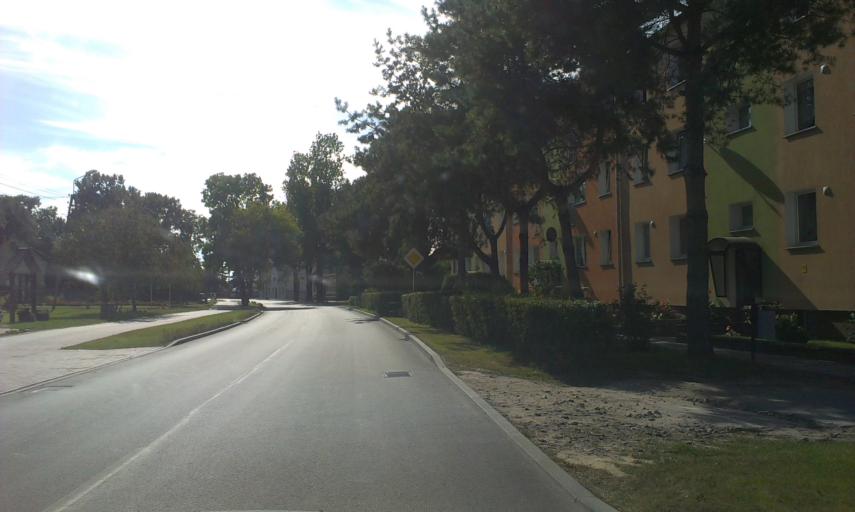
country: PL
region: Greater Poland Voivodeship
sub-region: Powiat pilski
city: Lobzenica
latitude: 53.2640
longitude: 17.2565
